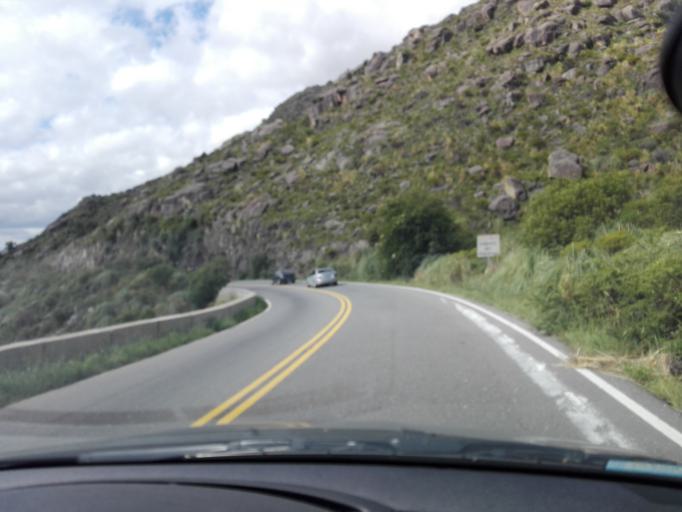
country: AR
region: Cordoba
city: Mina Clavero
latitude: -31.7659
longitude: -64.9200
